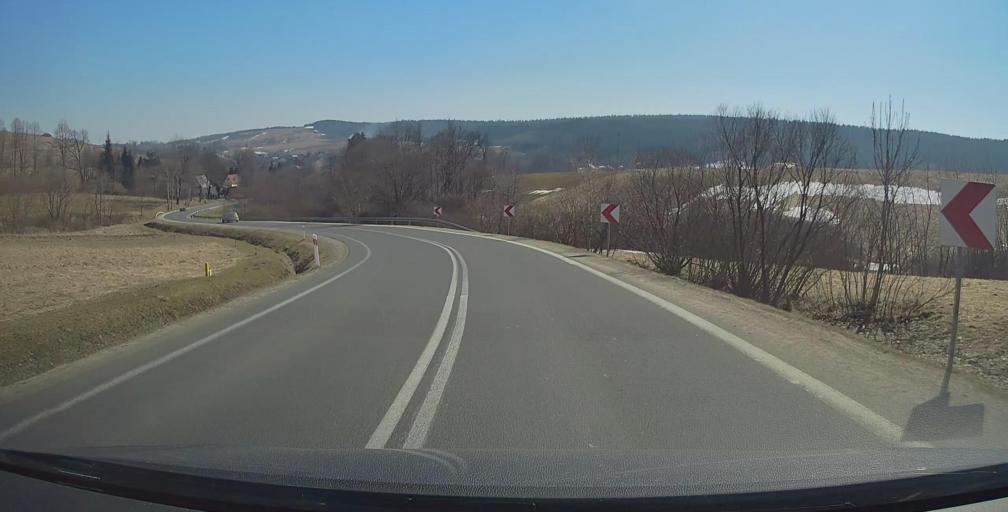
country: PL
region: Subcarpathian Voivodeship
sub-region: Powiat sanocki
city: Tyrawa Woloska
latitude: 49.6202
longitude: 22.4262
